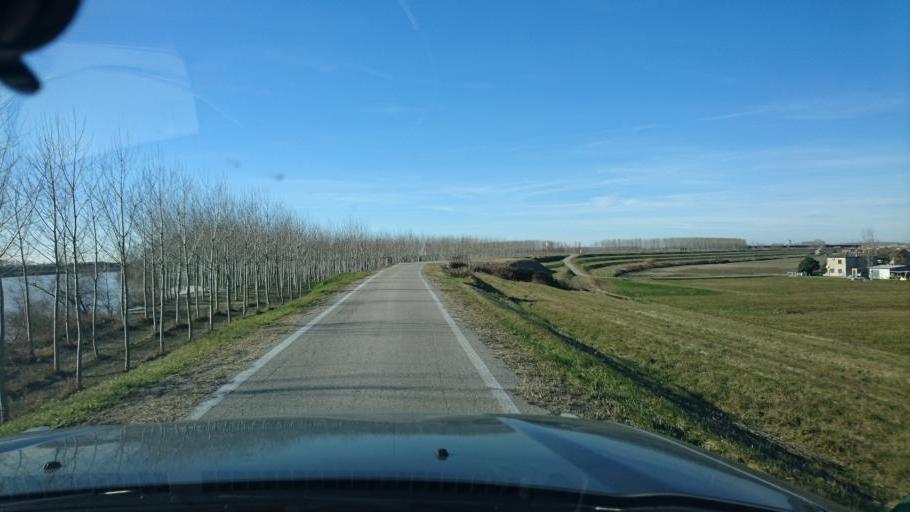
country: IT
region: Veneto
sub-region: Provincia di Rovigo
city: Ariano
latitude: 44.9331
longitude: 12.1345
